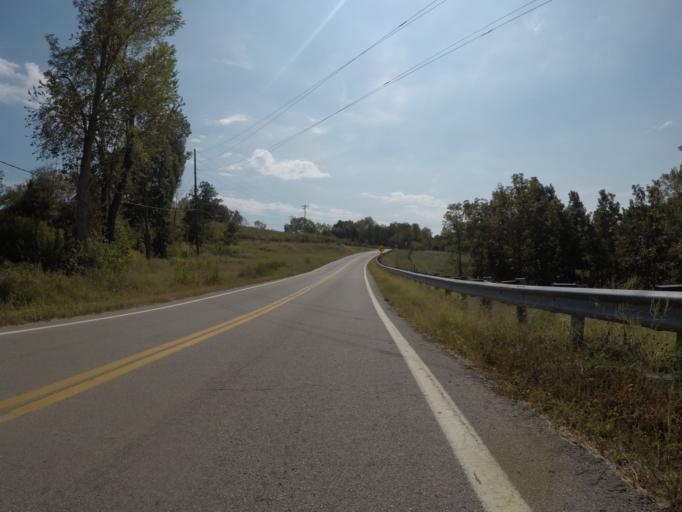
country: US
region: West Virginia
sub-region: Cabell County
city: Lesage
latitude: 38.5901
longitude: -82.4254
